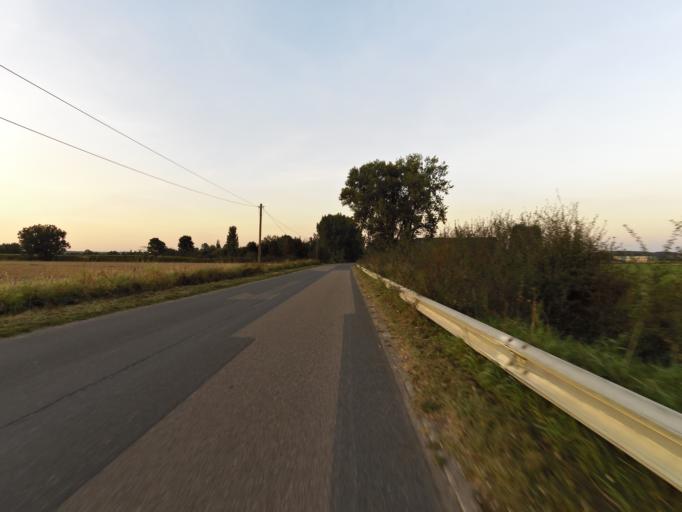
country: NL
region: Gelderland
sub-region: Gemeente Montferland
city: s-Heerenberg
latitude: 51.8563
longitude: 6.2655
